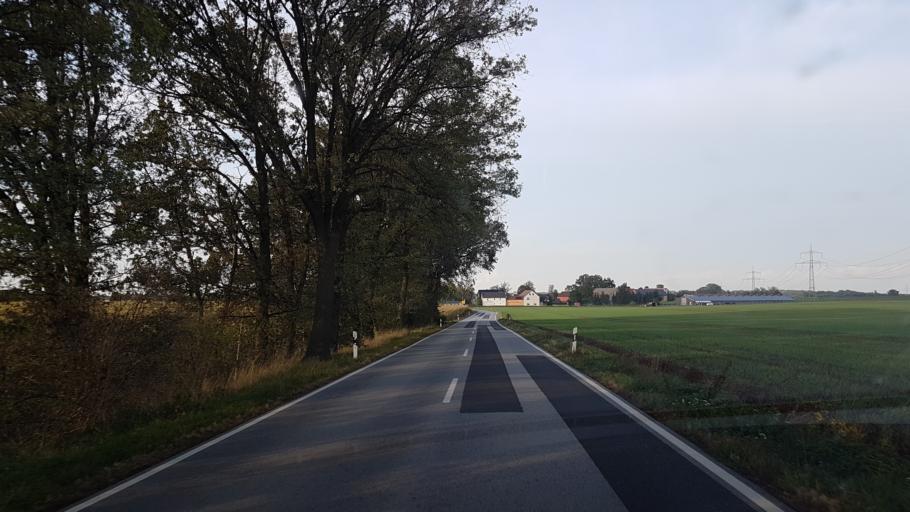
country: DE
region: Saxony
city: Crostwitz
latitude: 51.2151
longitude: 14.2339
